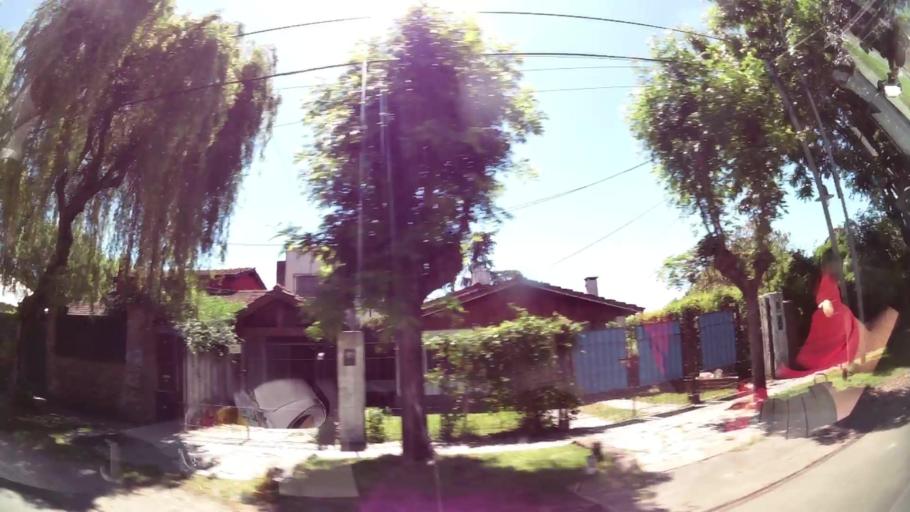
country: AR
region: Buenos Aires
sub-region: Partido de Tigre
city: Tigre
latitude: -34.4918
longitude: -58.6309
